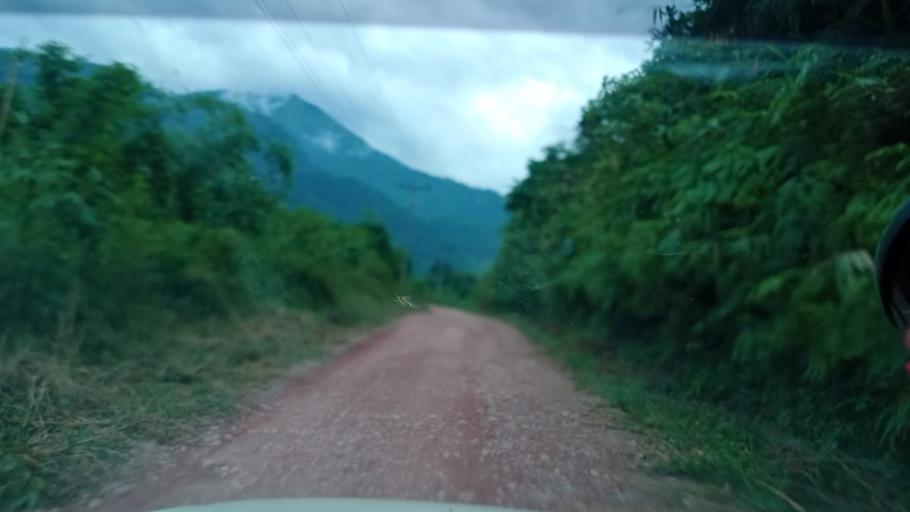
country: TH
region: Changwat Bueng Kan
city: Pak Khat
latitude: 18.7209
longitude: 103.2323
